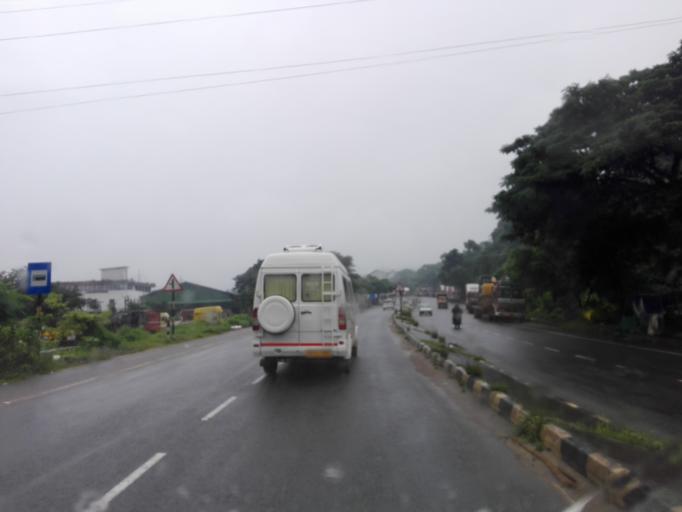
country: IN
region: Kerala
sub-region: Ernakulam
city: Elur
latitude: 10.0450
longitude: 76.3374
